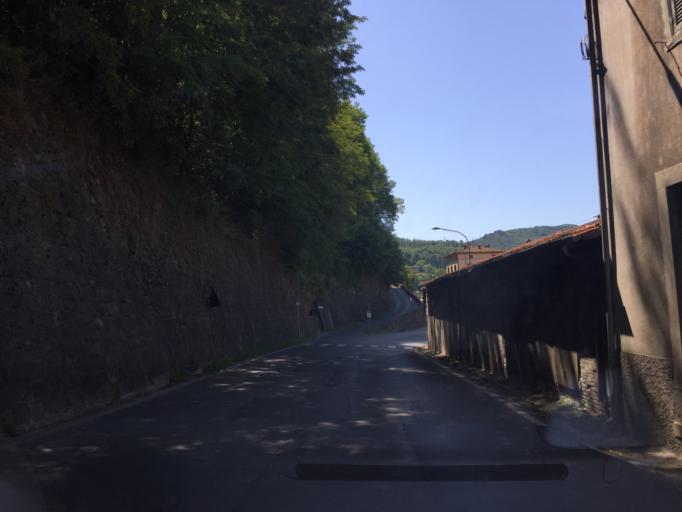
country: IT
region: Tuscany
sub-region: Provincia di Lucca
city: Castelnuovo di Garfagnana
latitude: 44.1160
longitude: 10.4102
